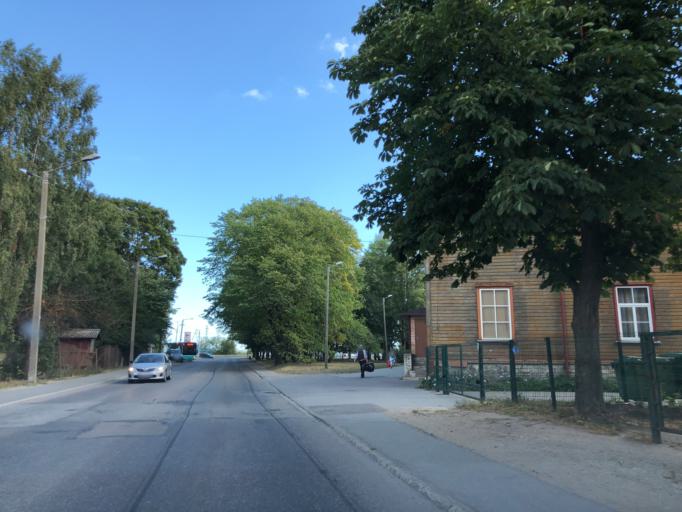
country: EE
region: Harju
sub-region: Tallinna linn
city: Tallinn
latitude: 59.4521
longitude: 24.7023
